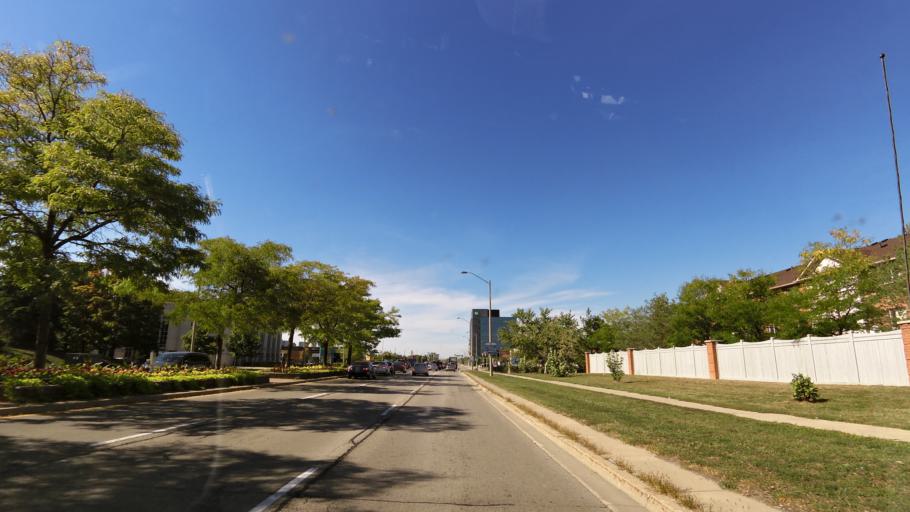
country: CA
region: Ontario
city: Brampton
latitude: 43.6573
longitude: -79.7214
